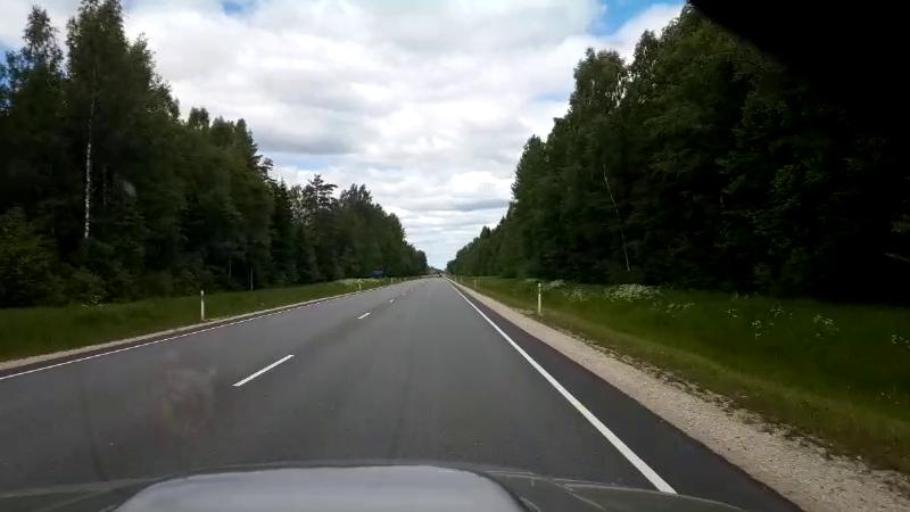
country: EE
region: Raplamaa
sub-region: Maerjamaa vald
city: Marjamaa
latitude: 58.7929
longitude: 24.4130
